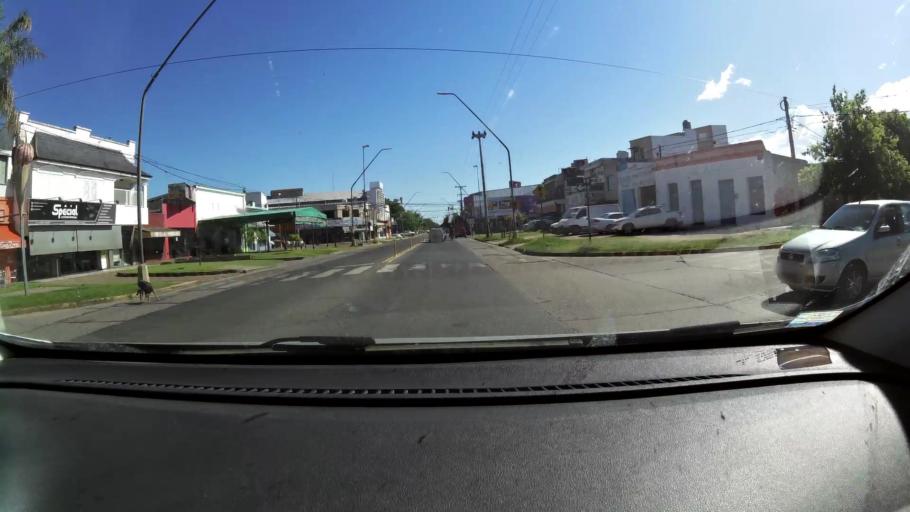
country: AR
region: Santa Fe
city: Santa Fe de la Vera Cruz
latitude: -31.6199
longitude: -60.6857
